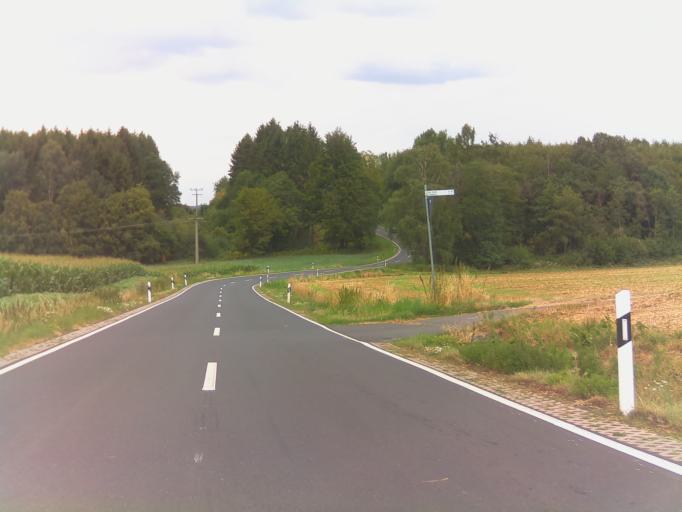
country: DE
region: Hesse
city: Gedern
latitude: 50.3979
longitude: 9.1983
